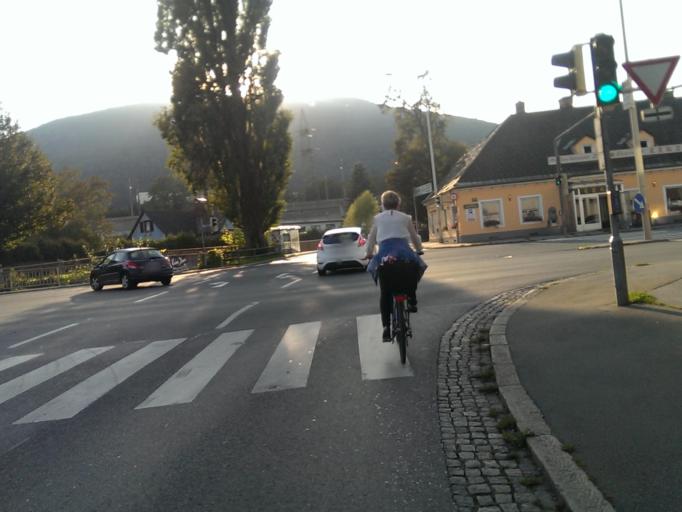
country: AT
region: Styria
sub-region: Graz Stadt
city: Goesting
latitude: 47.0961
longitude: 15.4047
